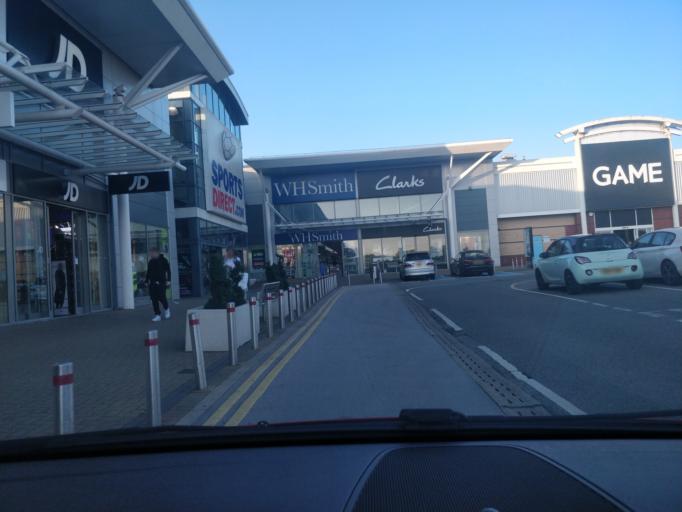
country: GB
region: England
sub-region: Lancashire
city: Preston
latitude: 53.7745
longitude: -2.6779
